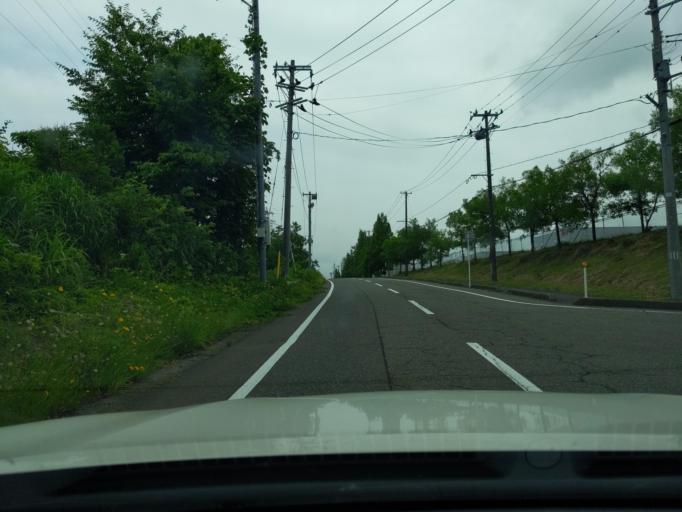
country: JP
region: Niigata
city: Kashiwazaki
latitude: 37.3430
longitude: 138.5964
